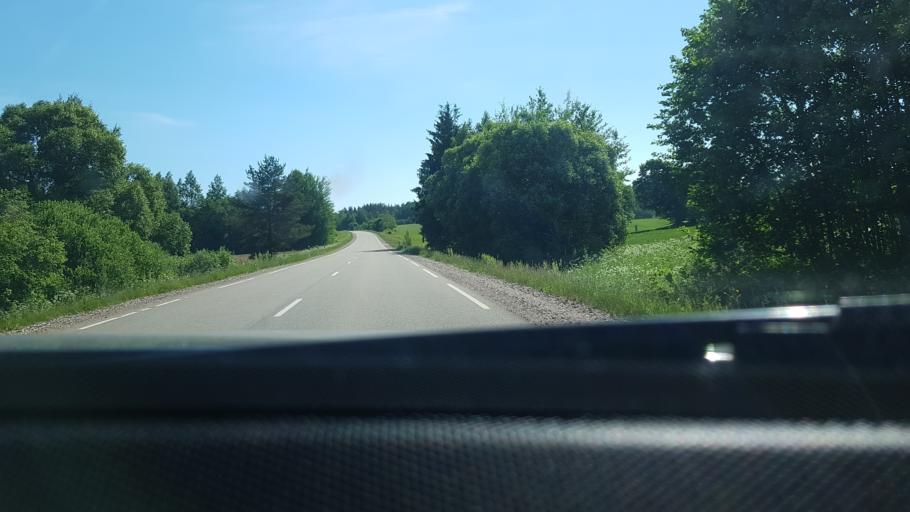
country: BY
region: Vitebsk
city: Braslaw
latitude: 55.8333
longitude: 26.9239
